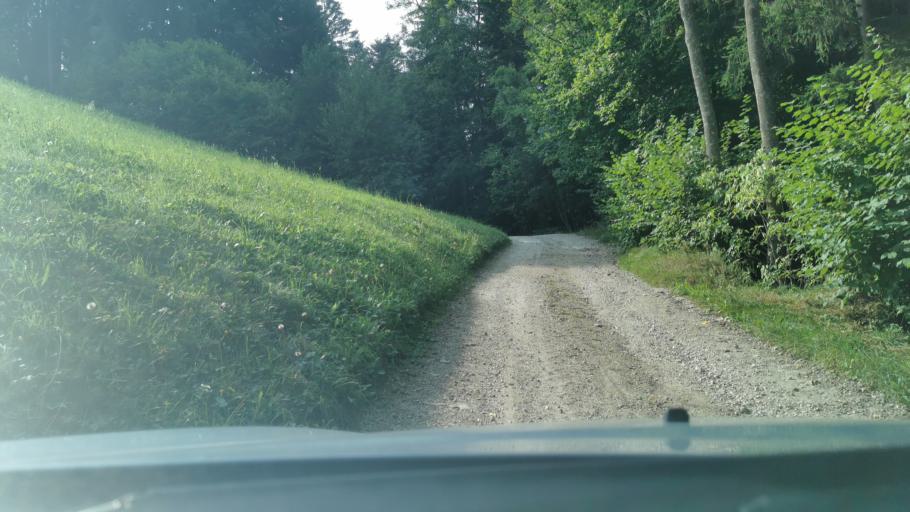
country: AT
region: Styria
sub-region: Politischer Bezirk Weiz
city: Fischbach
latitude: 47.4089
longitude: 15.6370
